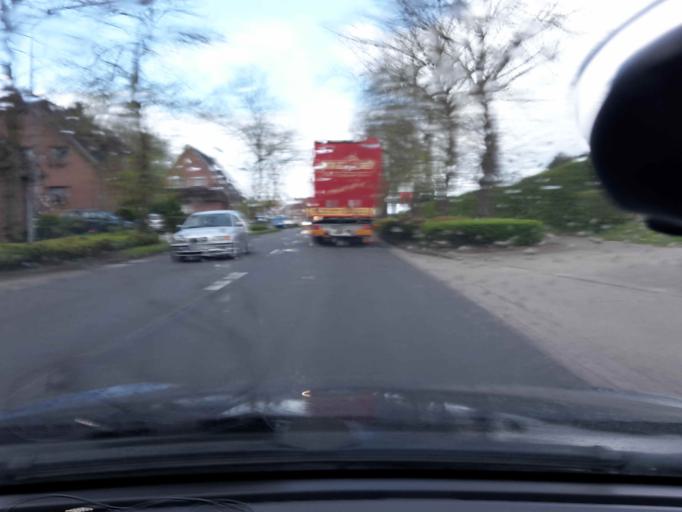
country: DE
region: Lower Saxony
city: Nottensdorf
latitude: 53.4828
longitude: 9.6294
